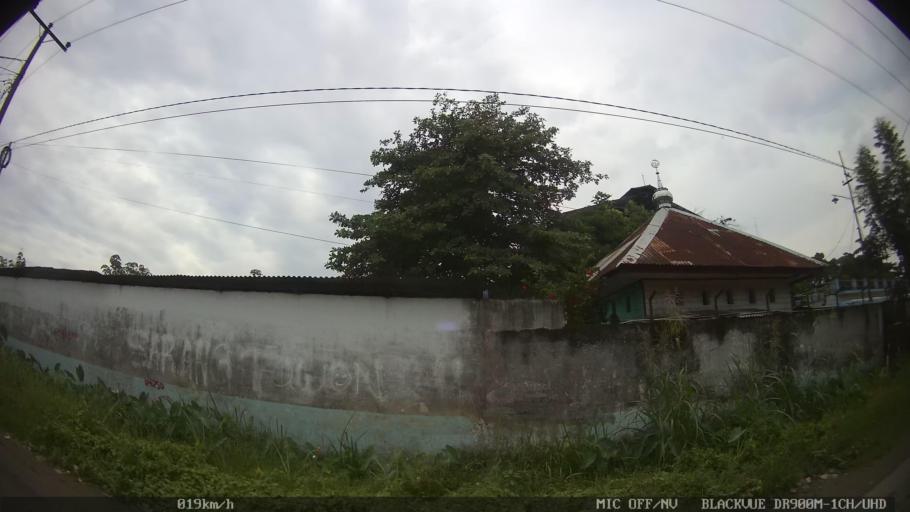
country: ID
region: North Sumatra
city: Sunggal
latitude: 3.6058
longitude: 98.6048
